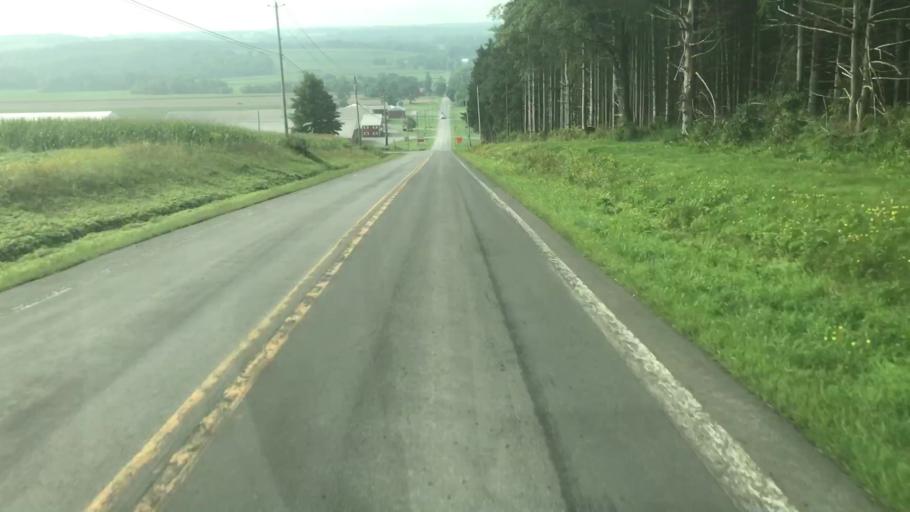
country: US
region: New York
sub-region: Onondaga County
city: Skaneateles
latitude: 42.8659
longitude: -76.4486
